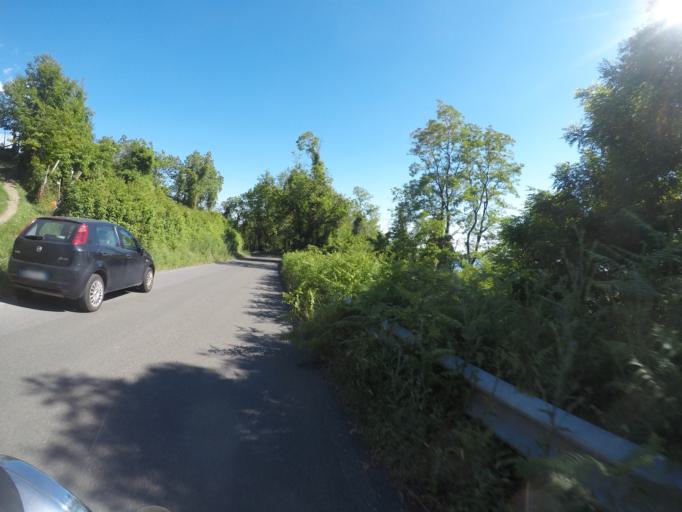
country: IT
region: Liguria
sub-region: Provincia di La Spezia
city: Casano-Dogana-Isola
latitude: 44.1152
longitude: 10.0676
